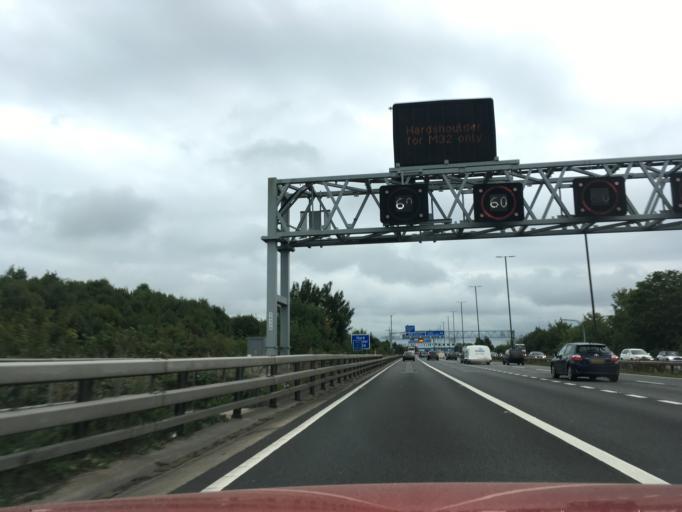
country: GB
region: England
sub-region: South Gloucestershire
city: Stoke Gifford
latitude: 51.5233
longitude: -2.5256
